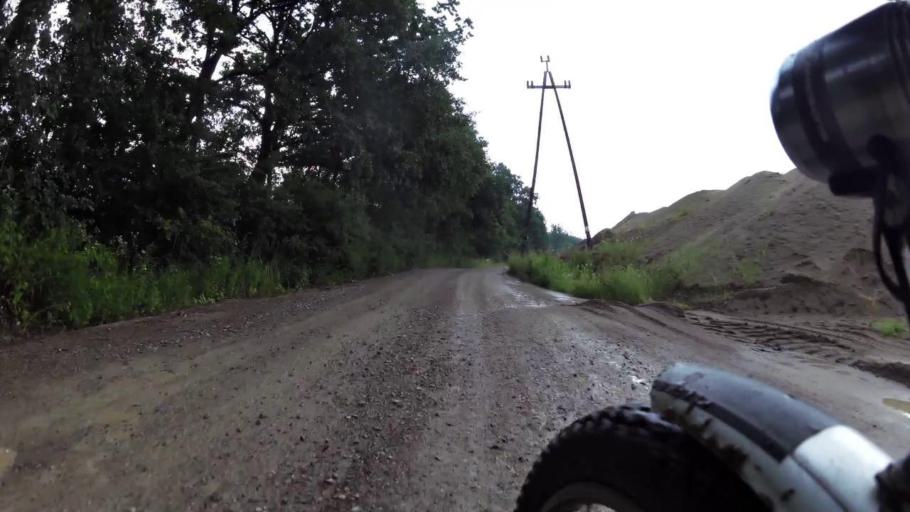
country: PL
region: West Pomeranian Voivodeship
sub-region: Powiat swidwinski
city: Swidwin
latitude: 53.7256
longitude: 15.6875
